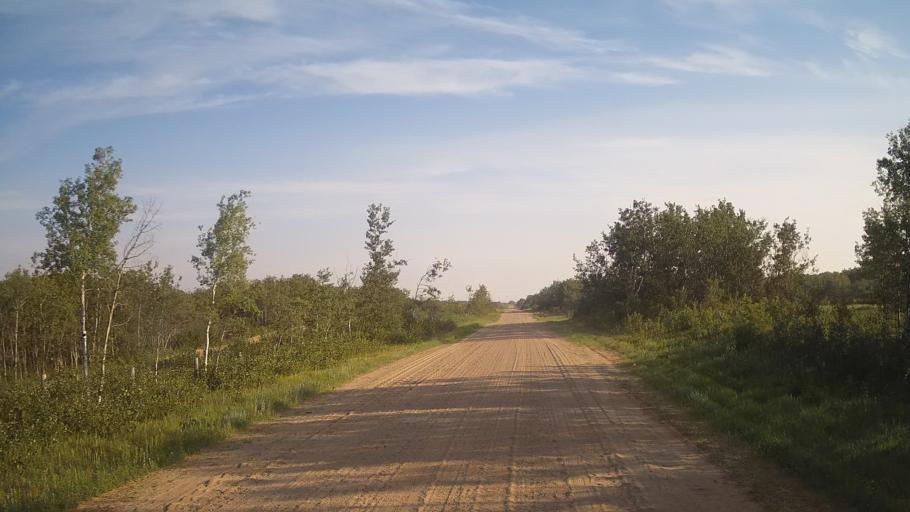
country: CA
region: Saskatchewan
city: Saskatoon
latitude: 51.8460
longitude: -106.5238
